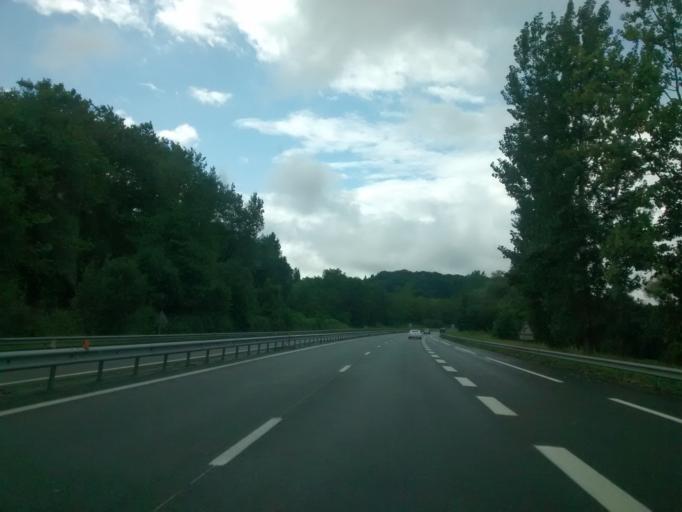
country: FR
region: Aquitaine
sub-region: Departement des Pyrenees-Atlantiques
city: Bardos
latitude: 43.5085
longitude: -1.2246
